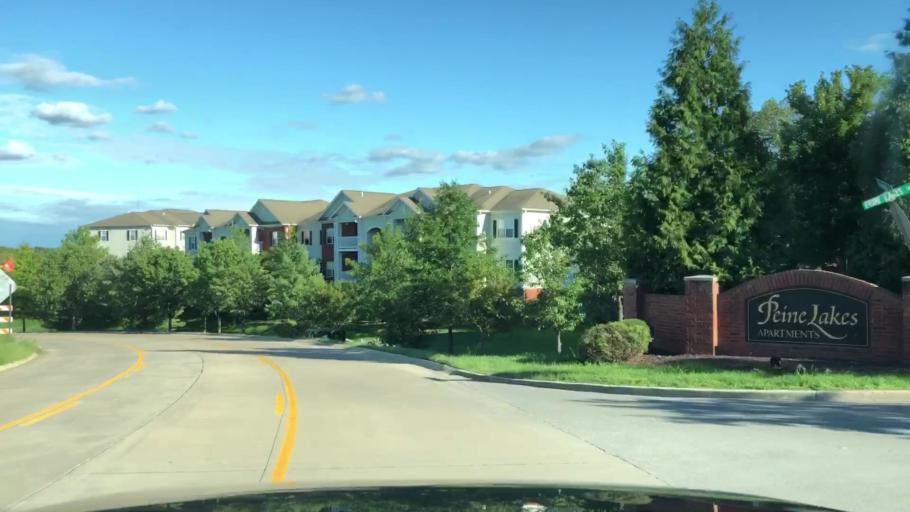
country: US
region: Missouri
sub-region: Saint Charles County
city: Wentzville
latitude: 38.8532
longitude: -90.8727
